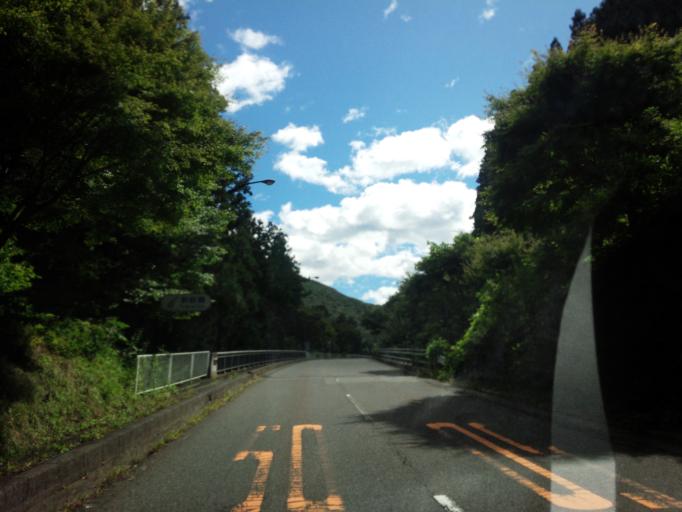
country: JP
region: Gunma
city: Nakanojomachi
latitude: 36.6861
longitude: 138.7721
